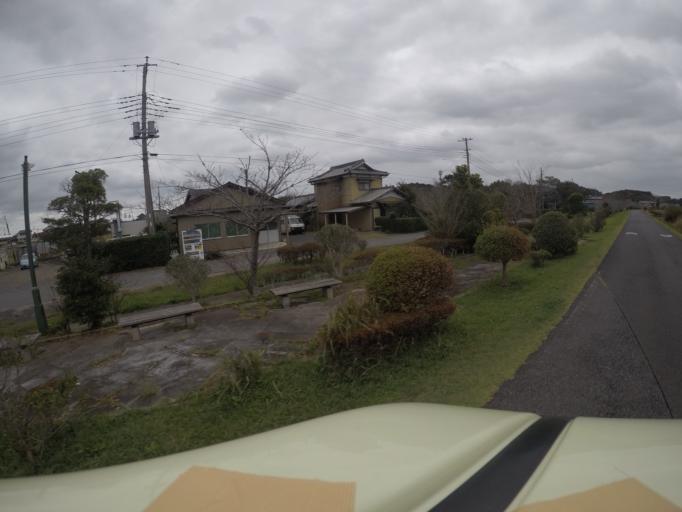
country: JP
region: Ibaraki
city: Itako
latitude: 35.9803
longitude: 140.4947
